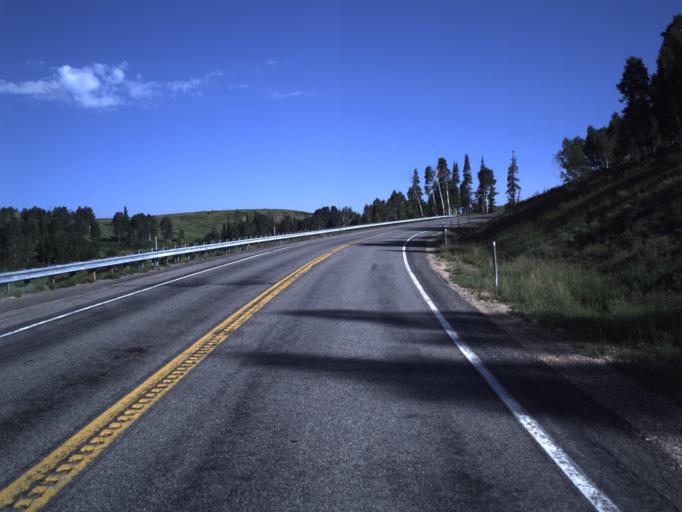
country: US
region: Utah
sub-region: Sanpete County
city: Fairview
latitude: 39.6080
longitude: -111.2795
